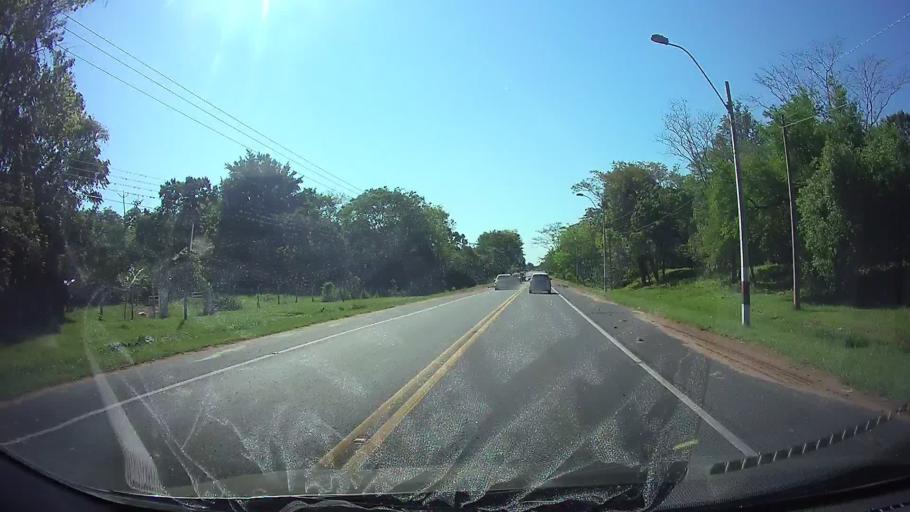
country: PY
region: Central
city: Aregua
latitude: -25.3232
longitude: -57.3673
